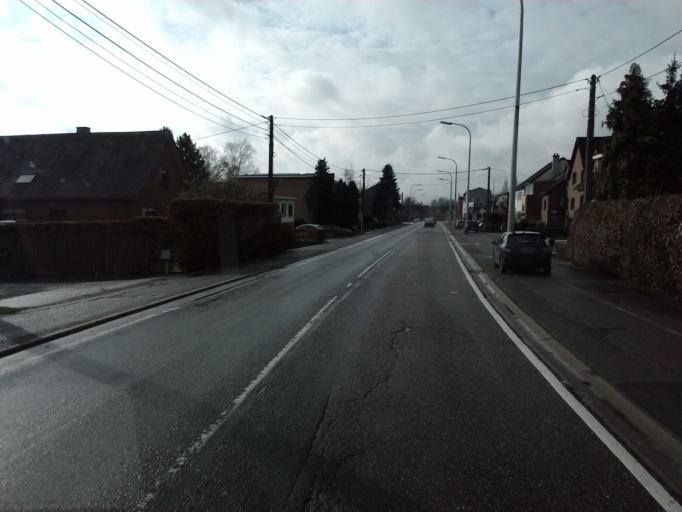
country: BE
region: Wallonia
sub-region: Province de Liege
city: Eupen
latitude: 50.6372
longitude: 6.0408
